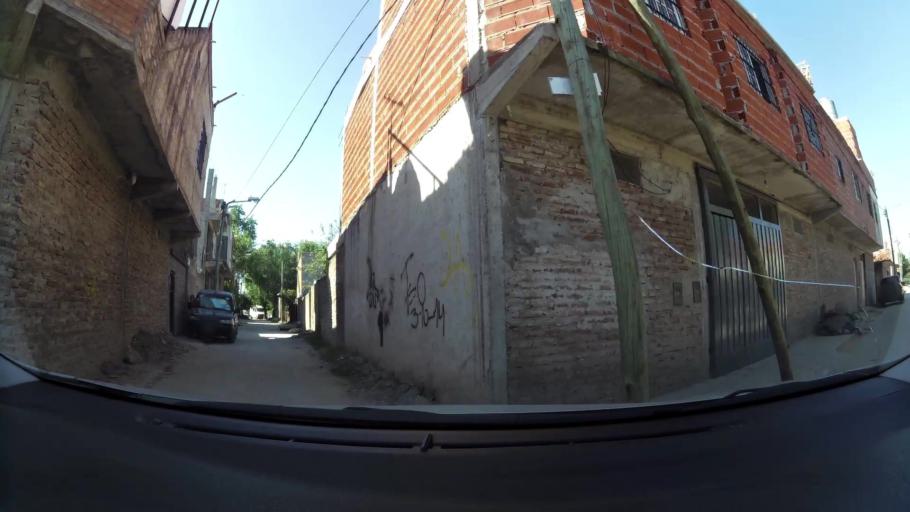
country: AR
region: Buenos Aires F.D.
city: Villa Lugano
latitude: -34.7103
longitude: -58.4794
